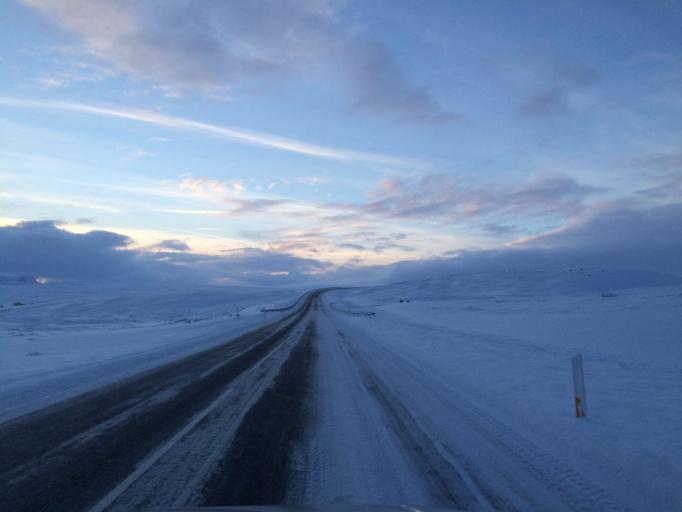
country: IS
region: South
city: Hveragerdi
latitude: 64.2264
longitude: -21.2100
